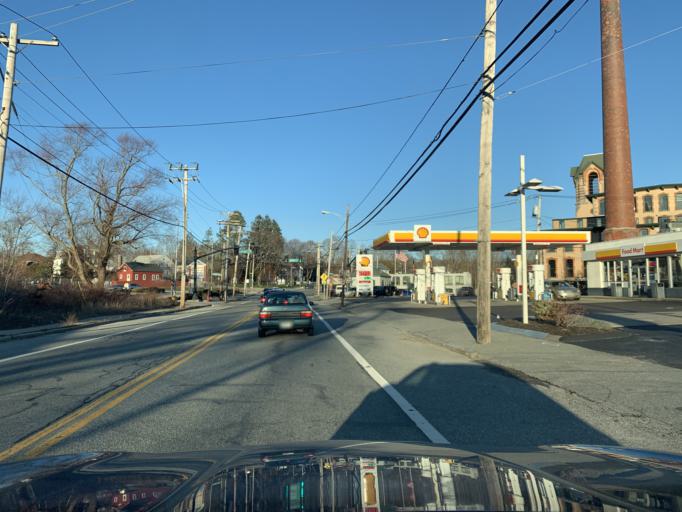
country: US
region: Rhode Island
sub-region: Kent County
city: West Warwick
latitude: 41.6957
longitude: -71.5480
